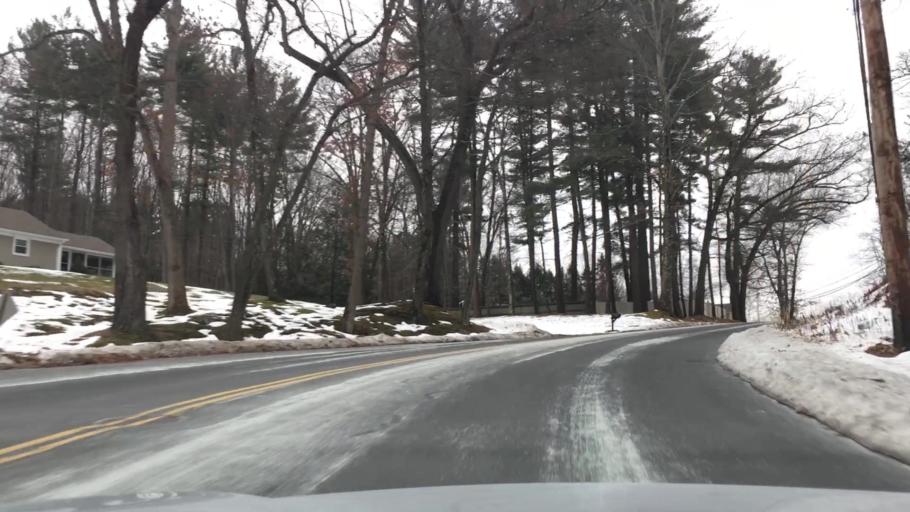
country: US
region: Massachusetts
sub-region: Hampden County
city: Westfield
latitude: 42.0967
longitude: -72.7113
